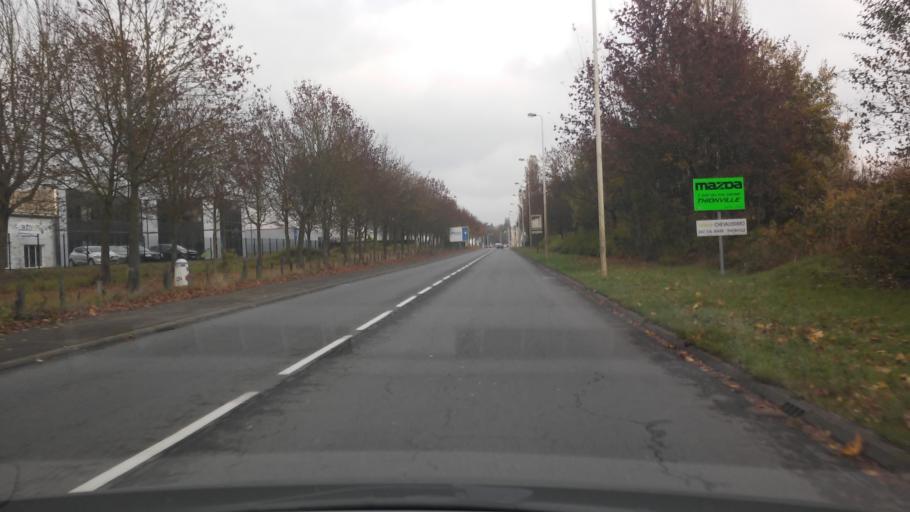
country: FR
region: Lorraine
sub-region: Departement de la Moselle
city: Terville
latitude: 49.3391
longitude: 6.1595
